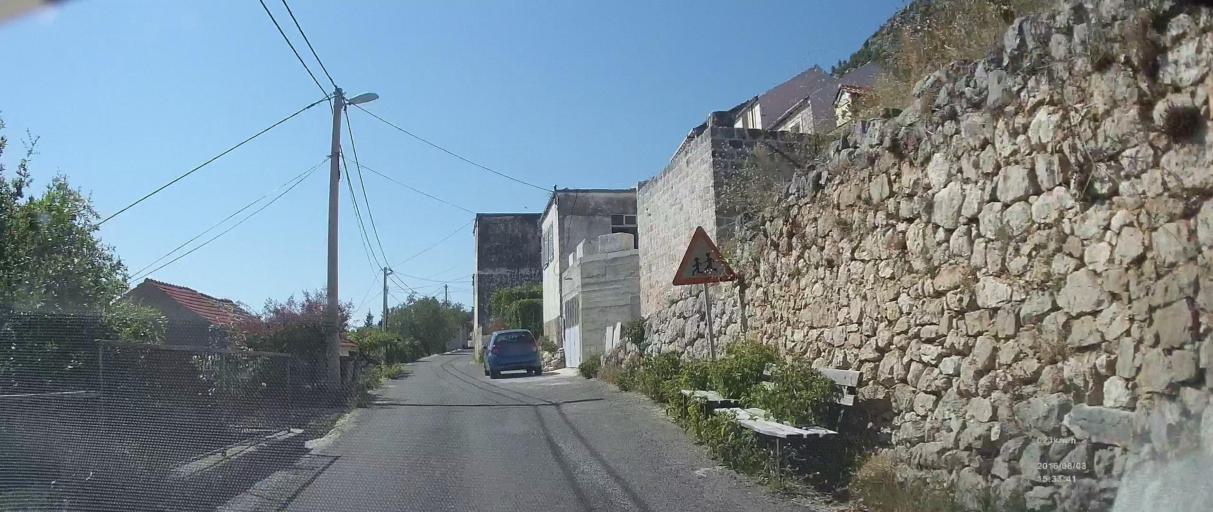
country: HR
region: Dubrovacko-Neretvanska
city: Blato
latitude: 42.7347
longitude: 17.5536
